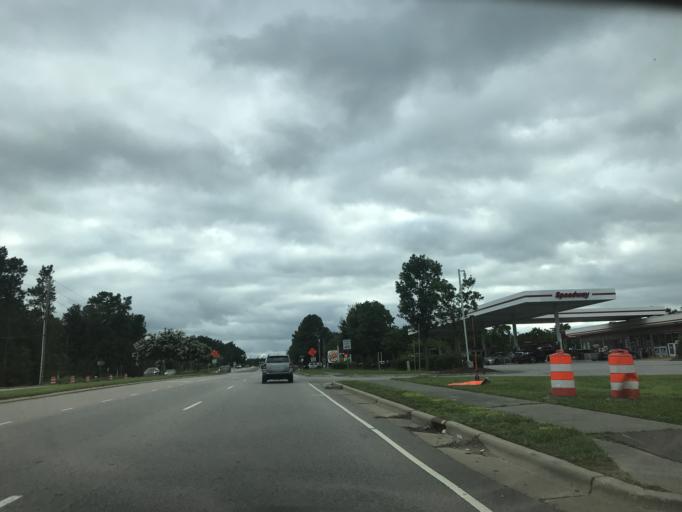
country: US
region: North Carolina
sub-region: Wake County
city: Garner
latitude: 35.7260
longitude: -78.5802
